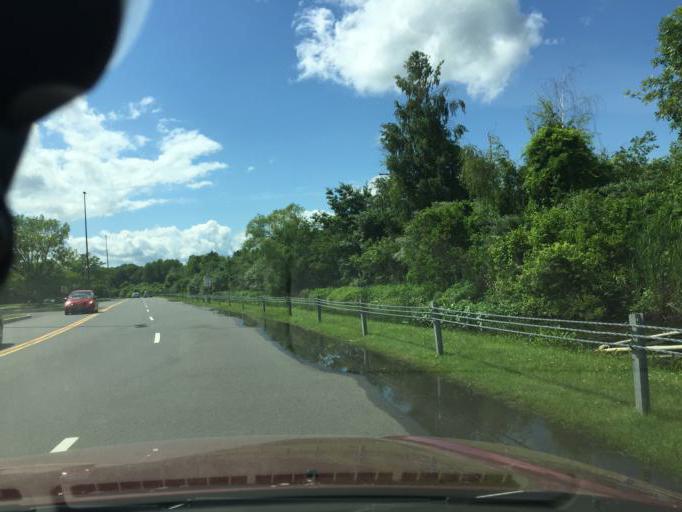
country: US
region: Connecticut
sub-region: Fairfield County
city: Danbury
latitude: 41.3823
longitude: -73.4770
